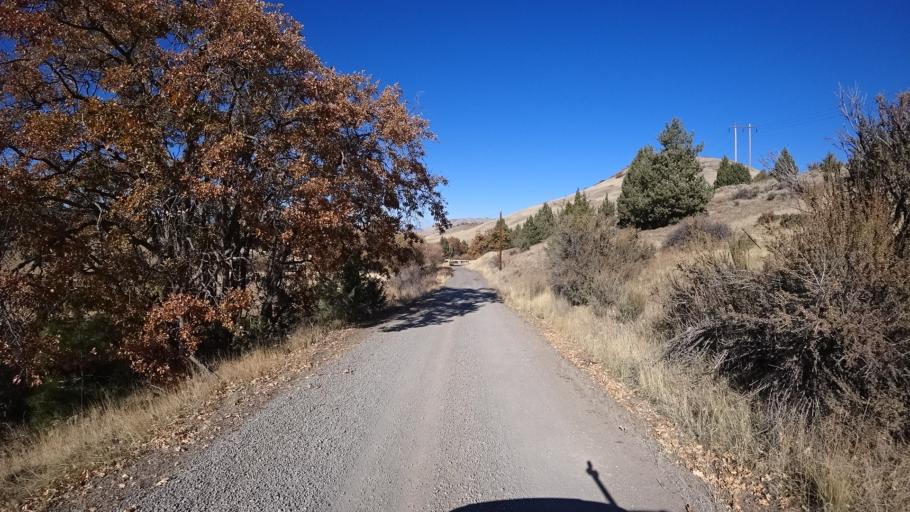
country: US
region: California
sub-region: Siskiyou County
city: Montague
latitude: 41.7900
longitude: -122.3602
